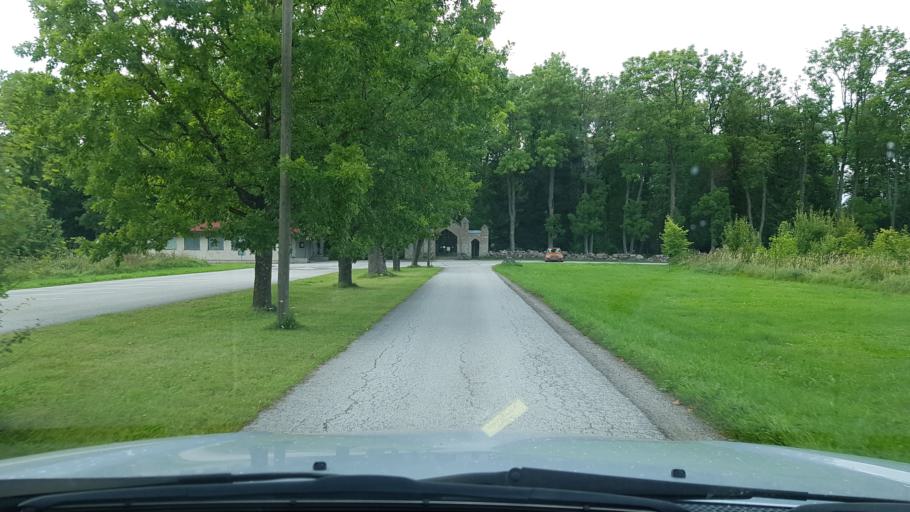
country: EE
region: Harju
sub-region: Rae vald
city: Jueri
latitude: 59.3601
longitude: 24.9208
